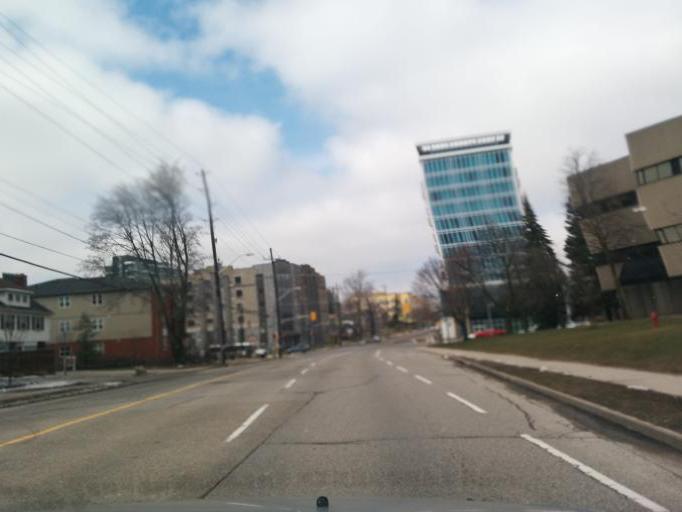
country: CA
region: Ontario
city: Waterloo
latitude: 43.4730
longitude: -80.5308
